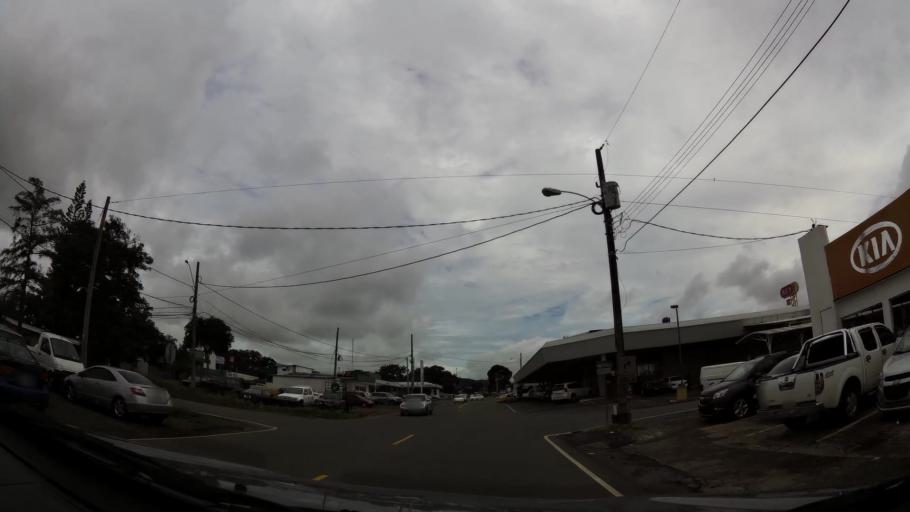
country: PA
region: Chiriqui
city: David
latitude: 8.4445
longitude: -82.4225
